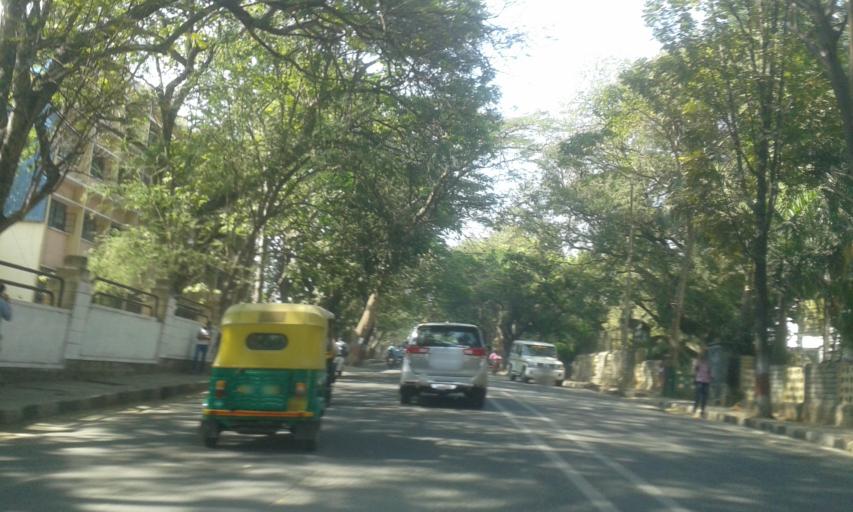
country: IN
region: Karnataka
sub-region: Bangalore Urban
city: Bangalore
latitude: 13.0096
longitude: 77.5710
